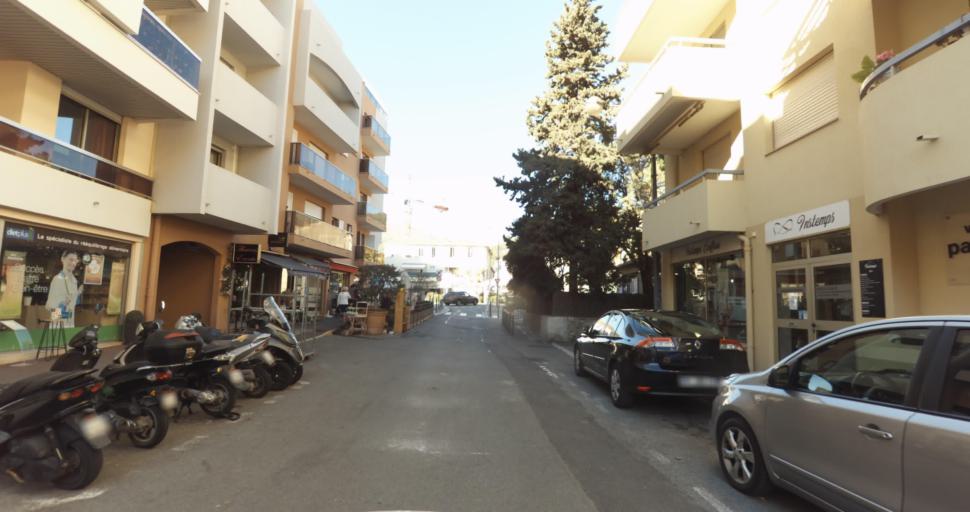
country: FR
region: Provence-Alpes-Cote d'Azur
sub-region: Departement des Alpes-Maritimes
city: Vence
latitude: 43.7242
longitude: 7.1077
